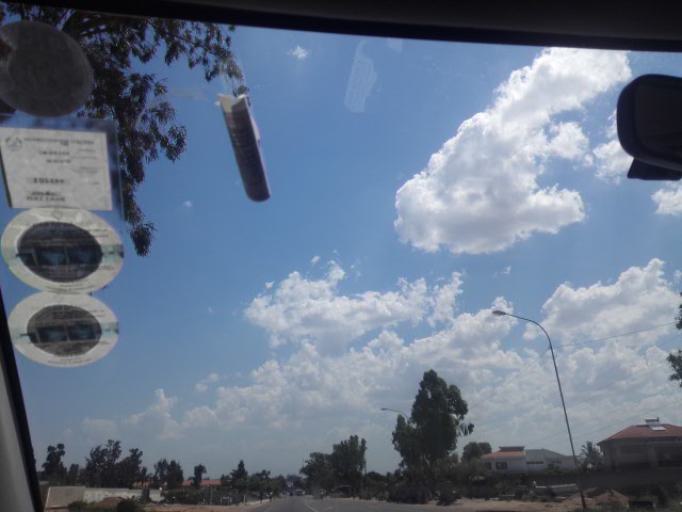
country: MZ
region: Maputo
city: Matola
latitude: -25.9677
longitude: 32.4437
